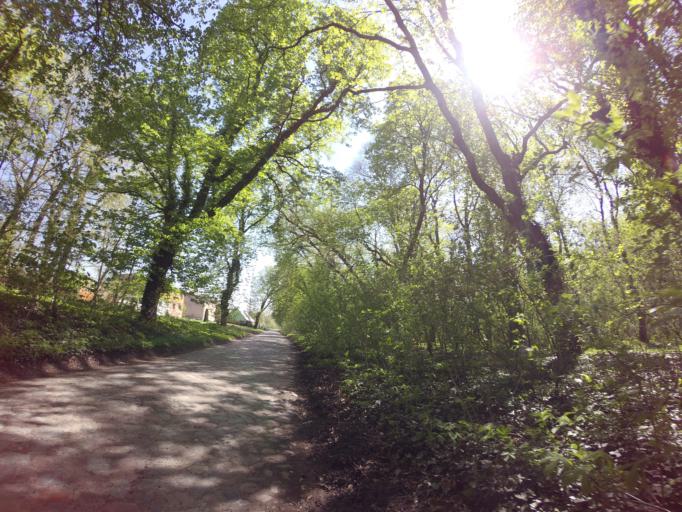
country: PL
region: West Pomeranian Voivodeship
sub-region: Powiat choszczenski
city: Choszczno
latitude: 53.1809
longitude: 15.3223
